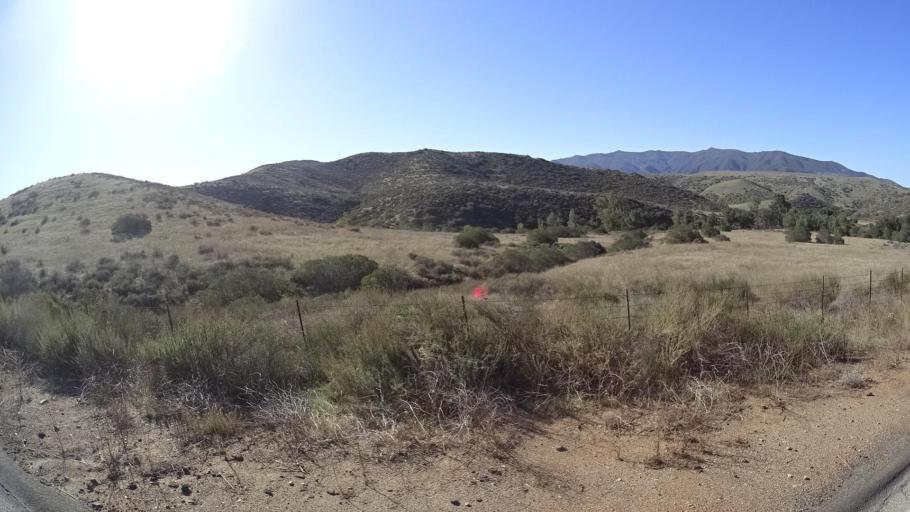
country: US
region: California
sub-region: San Diego County
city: Jamul
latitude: 32.6728
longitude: -116.8100
